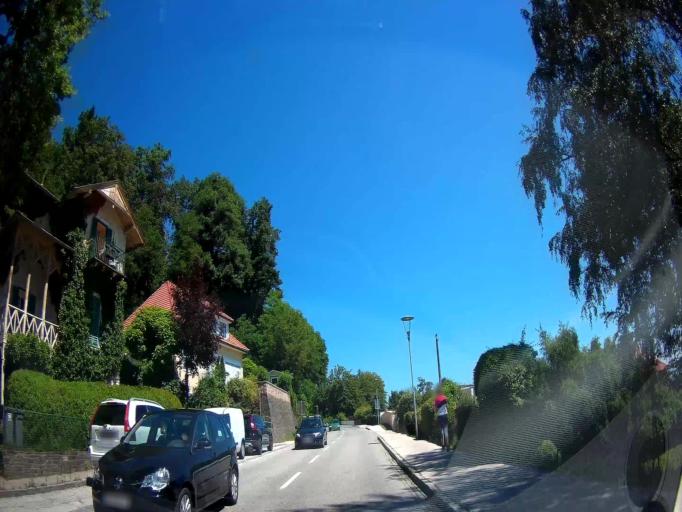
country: AT
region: Carinthia
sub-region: Politischer Bezirk Klagenfurt Land
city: Maria Worth
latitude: 46.6097
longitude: 14.1796
